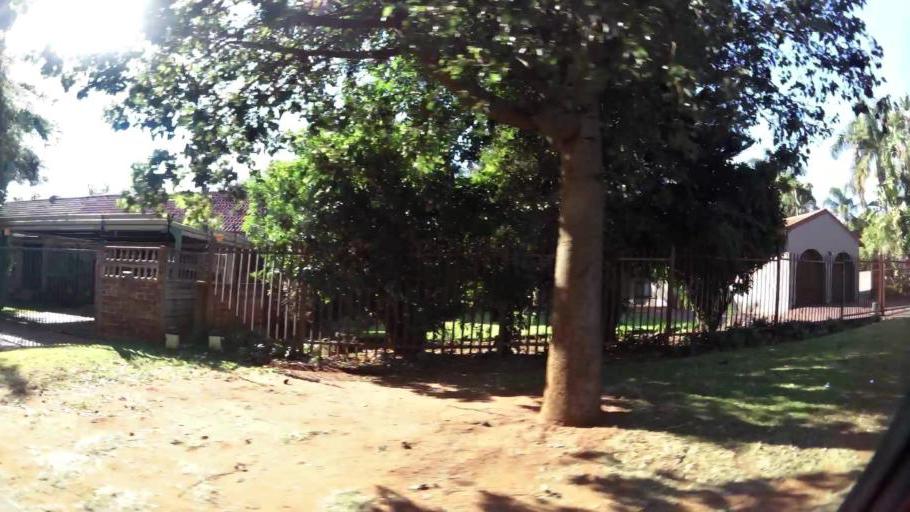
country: ZA
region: Gauteng
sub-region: City of Tshwane Metropolitan Municipality
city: Pretoria
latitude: -25.6686
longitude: 28.1431
